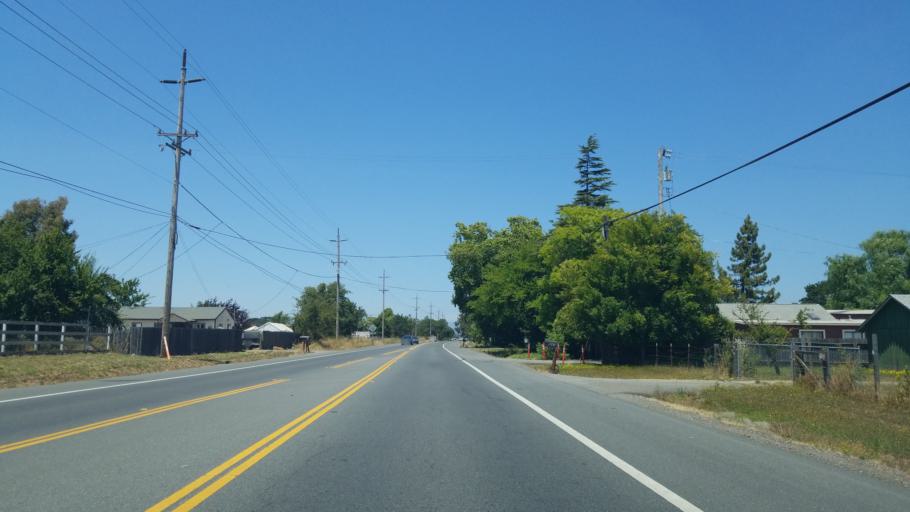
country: US
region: California
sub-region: Sonoma County
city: Rohnert Park
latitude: 38.3715
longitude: -122.7414
